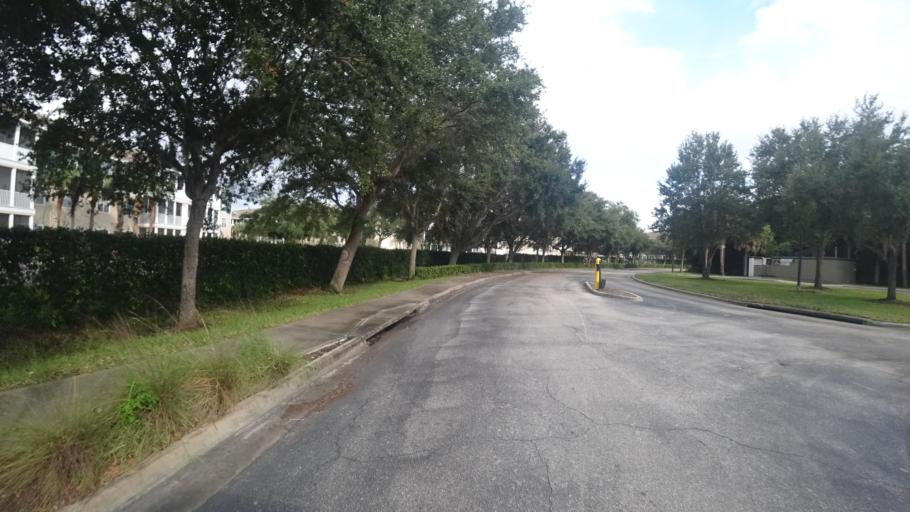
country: US
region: Florida
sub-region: Manatee County
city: South Bradenton
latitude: 27.4570
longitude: -82.6161
